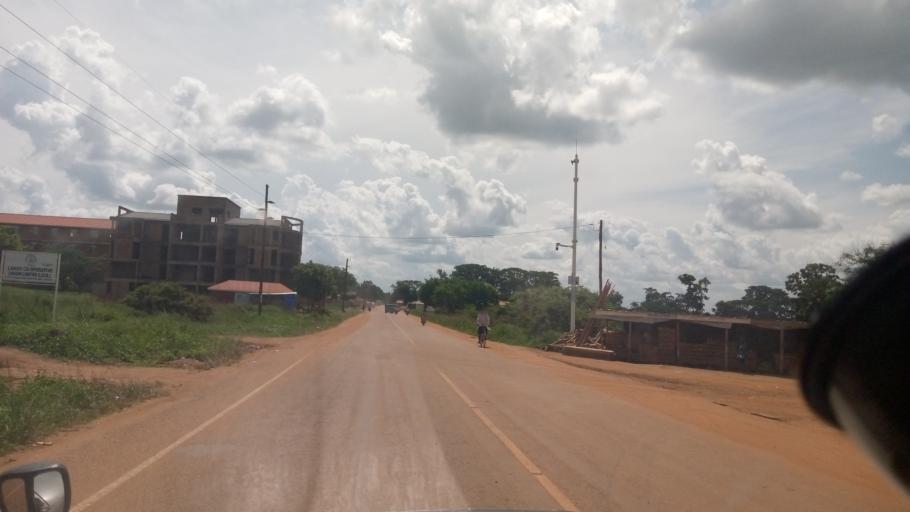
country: UG
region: Northern Region
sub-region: Lira District
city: Lira
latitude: 2.2483
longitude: 32.9052
